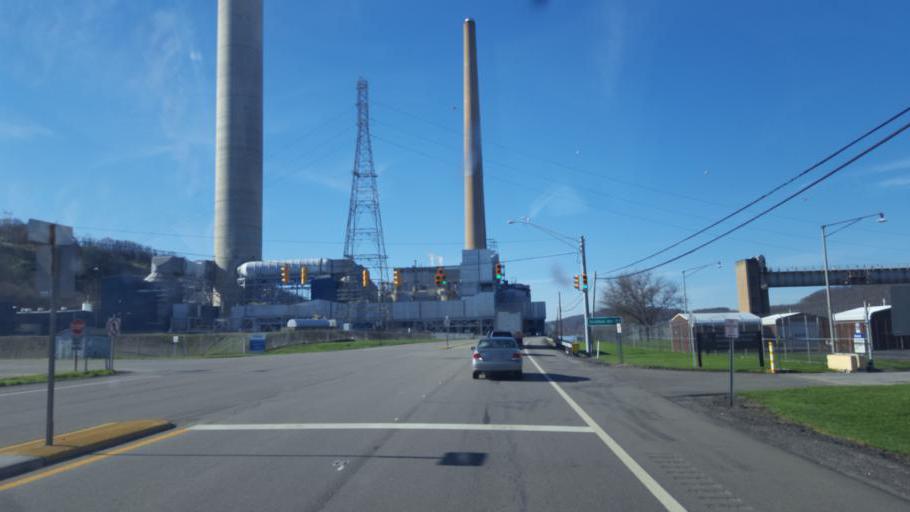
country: US
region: West Virginia
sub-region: Hancock County
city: New Cumberland
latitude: 40.5259
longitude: -80.6287
